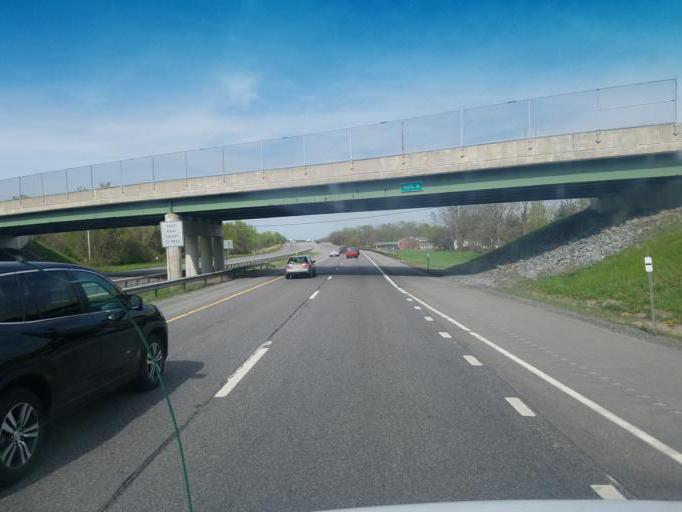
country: US
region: New York
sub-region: Cayuga County
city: Port Byron
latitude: 43.0391
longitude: -76.6321
